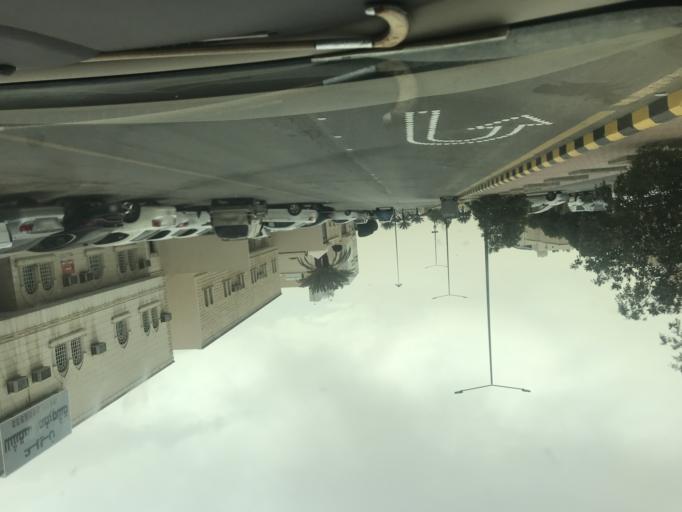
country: SA
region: Ar Riyad
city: Riyadh
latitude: 24.7361
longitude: 46.7532
